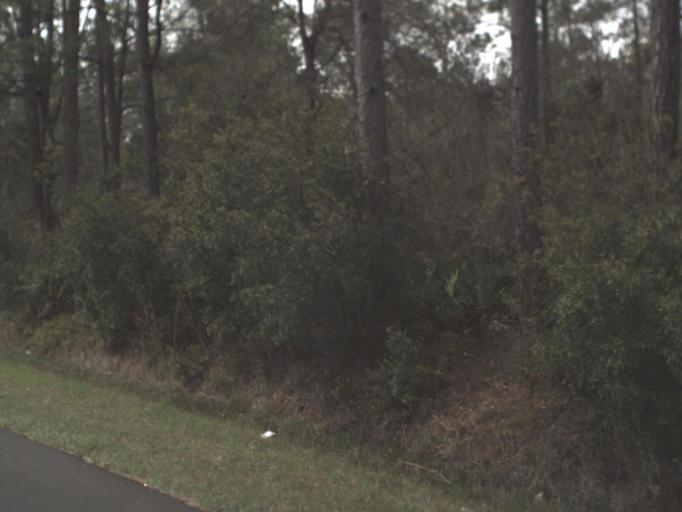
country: US
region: Florida
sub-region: Gadsden County
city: Midway
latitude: 30.3930
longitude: -84.6176
